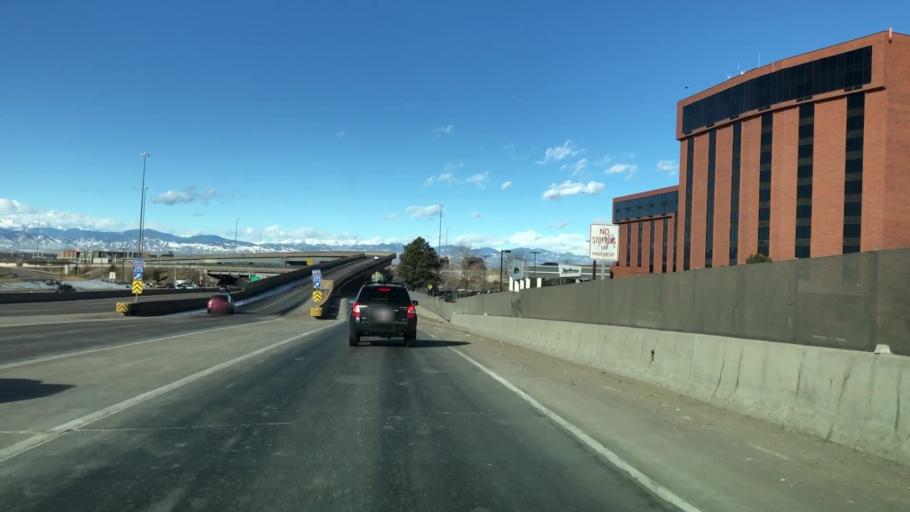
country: US
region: Colorado
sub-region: Adams County
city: Aurora
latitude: 39.6577
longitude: -104.8386
